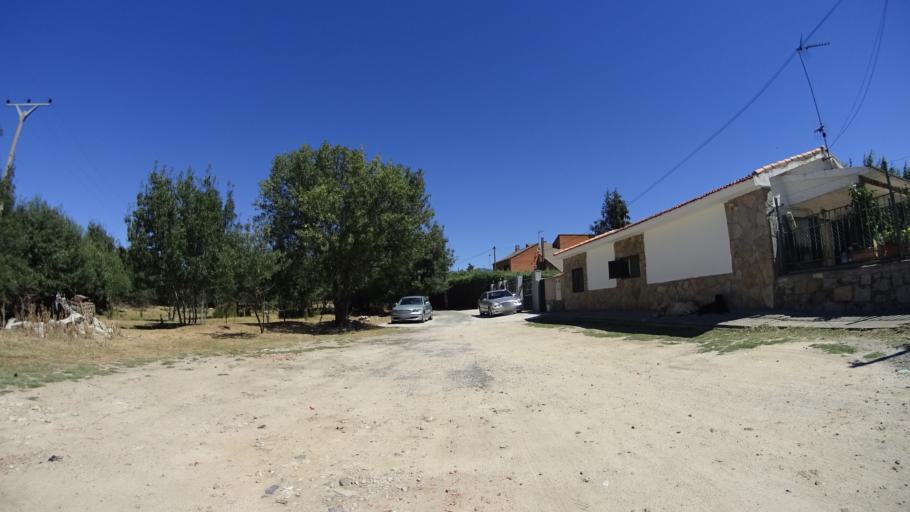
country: ES
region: Madrid
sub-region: Provincia de Madrid
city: Alpedrete
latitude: 40.6626
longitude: -4.0487
